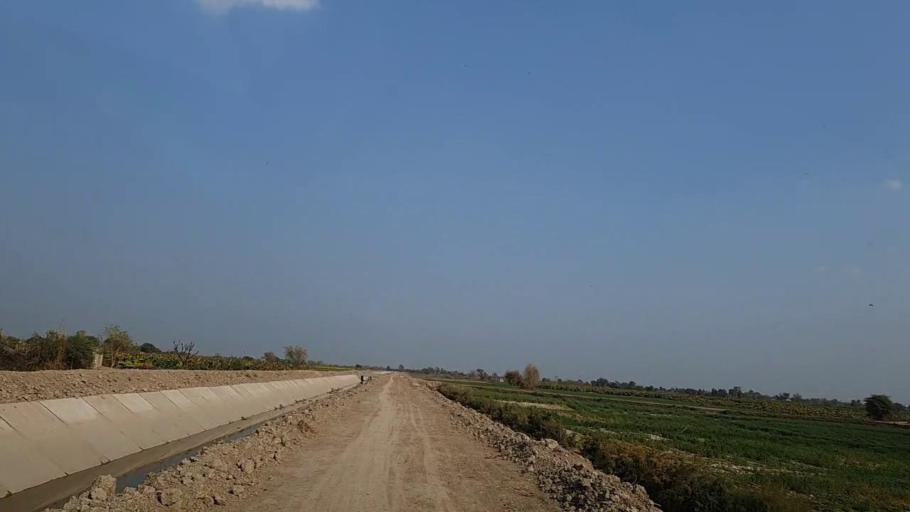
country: PK
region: Sindh
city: Nawabshah
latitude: 26.1490
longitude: 68.3983
